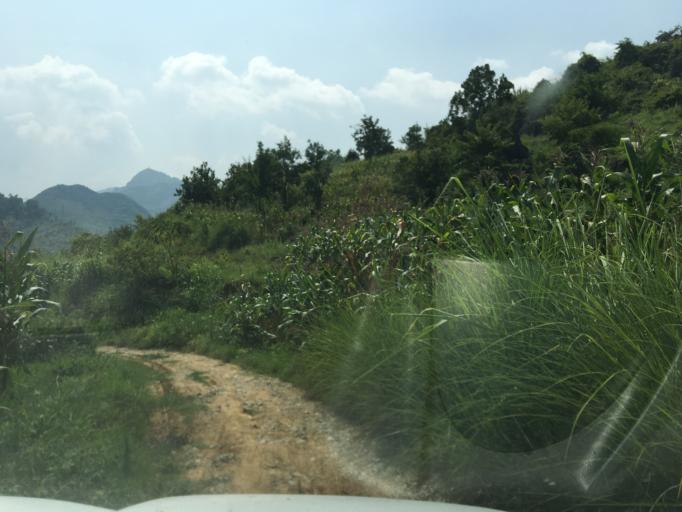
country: CN
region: Guangxi Zhuangzu Zizhiqu
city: Xinzhou
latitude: 24.9952
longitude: 105.7491
